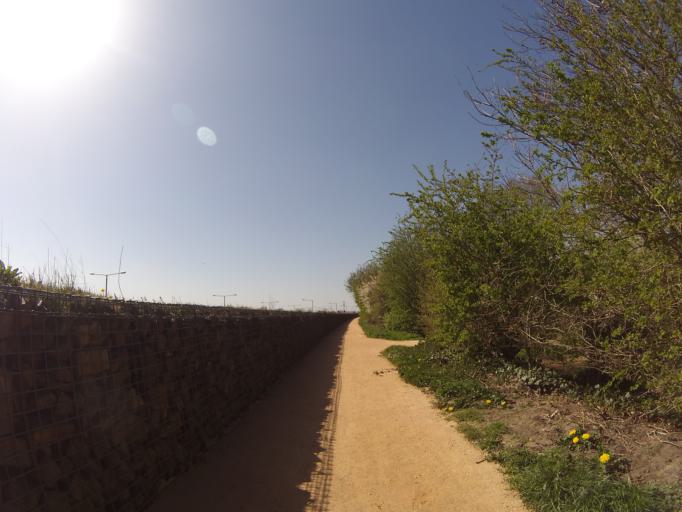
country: NL
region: Utrecht
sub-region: Gemeente Amersfoort
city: Hoogland
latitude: 52.1941
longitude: 5.3738
